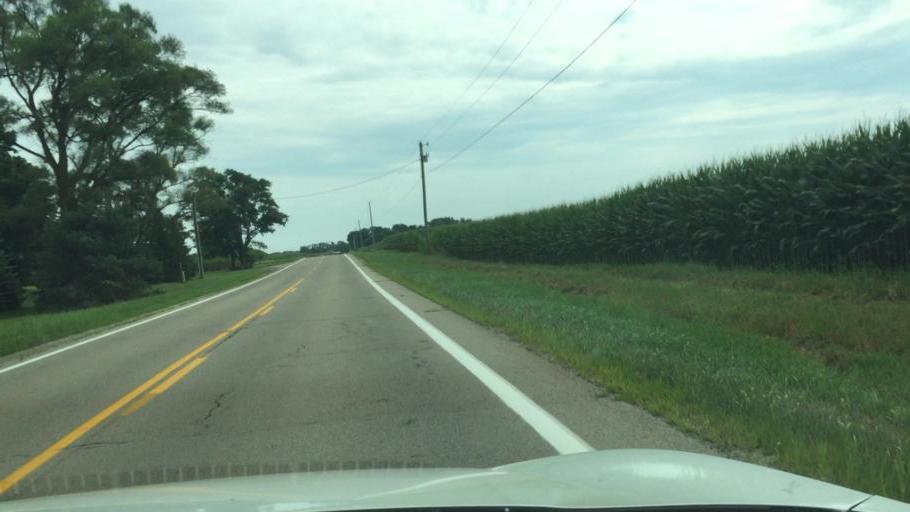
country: US
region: Ohio
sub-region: Champaign County
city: North Lewisburg
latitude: 40.1490
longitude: -83.5290
